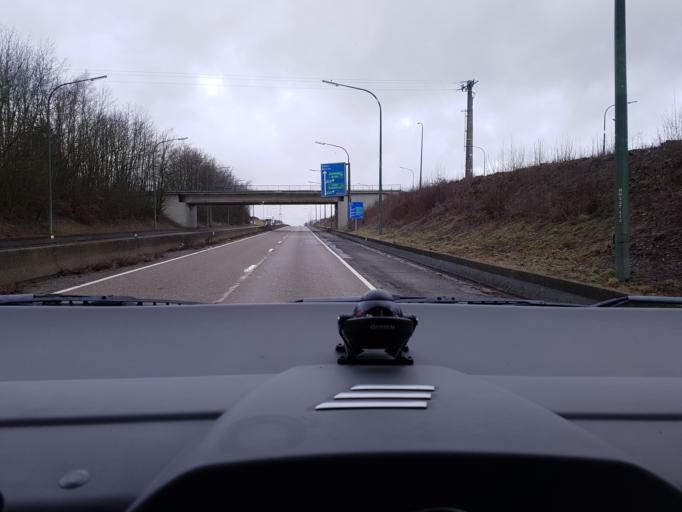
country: BE
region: Wallonia
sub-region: Province du Luxembourg
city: Bastogne
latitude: 49.9978
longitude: 5.6976
